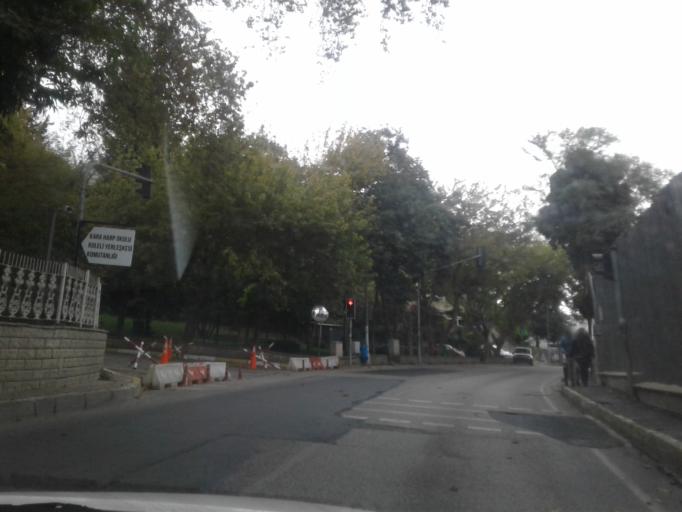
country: TR
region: Istanbul
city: UEskuedar
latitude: 41.0572
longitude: 29.0534
